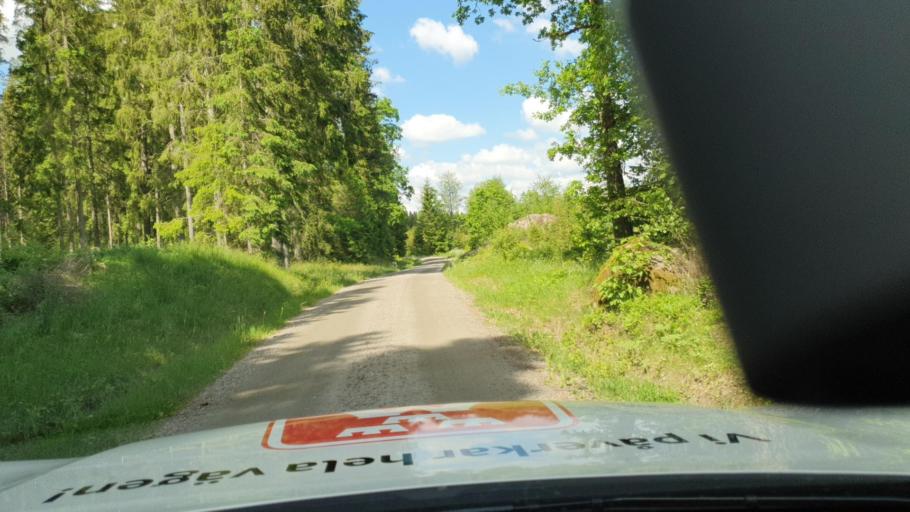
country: SE
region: Vaestra Goetaland
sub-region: Falkopings Kommun
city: Falkoeping
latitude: 58.0330
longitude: 13.6588
